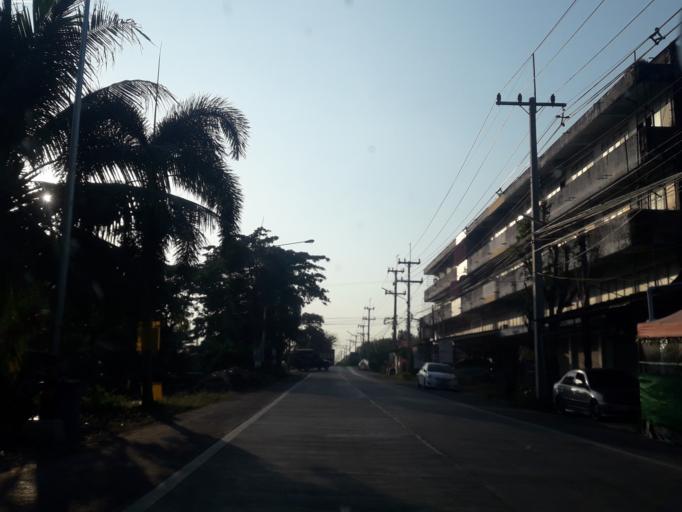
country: TH
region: Pathum Thani
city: Nong Suea
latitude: 14.1367
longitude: 100.8472
